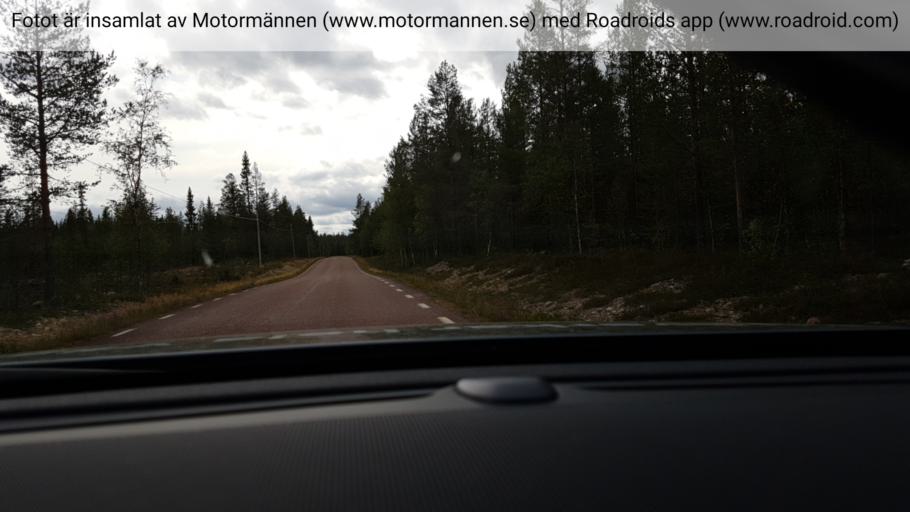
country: NO
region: Hedmark
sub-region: Trysil
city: Innbygda
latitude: 61.6964
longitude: 12.6275
